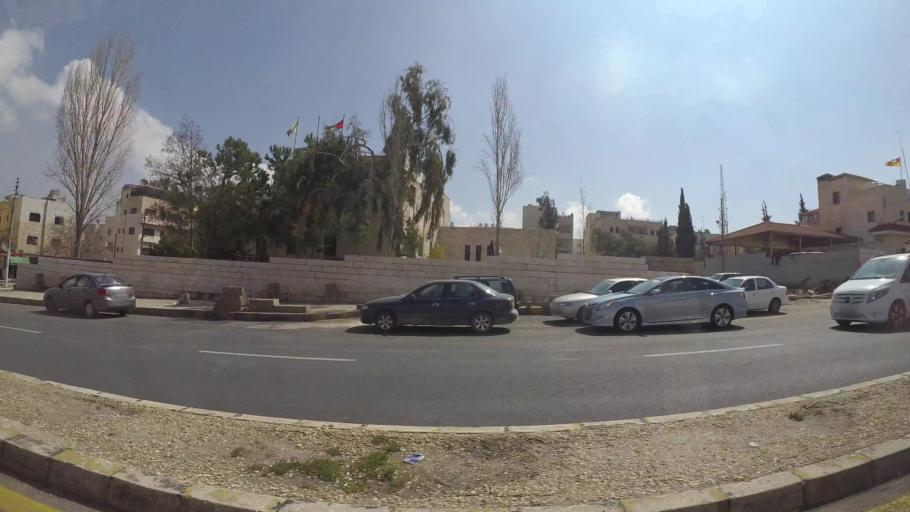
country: JO
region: Amman
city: Al Bunayyat ash Shamaliyah
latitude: 31.9285
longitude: 35.9025
